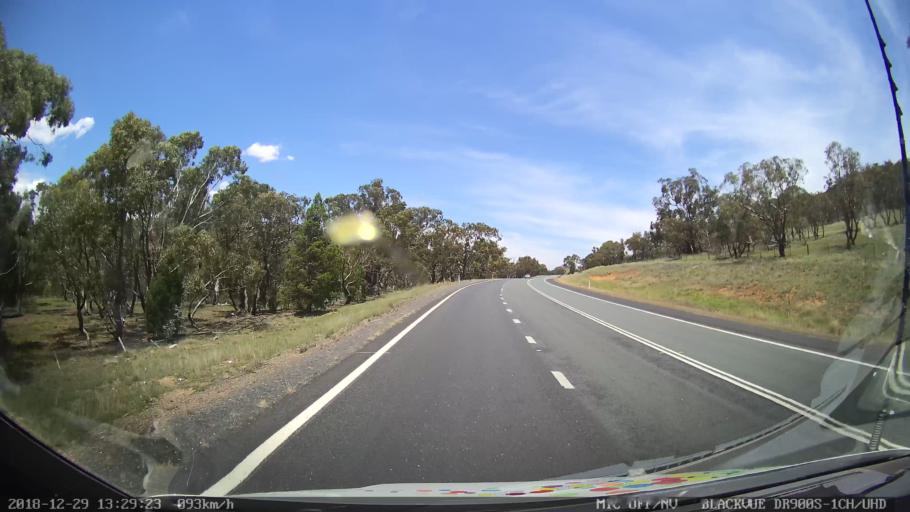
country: AU
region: New South Wales
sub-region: Cooma-Monaro
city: Cooma
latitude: -35.8893
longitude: 149.1618
